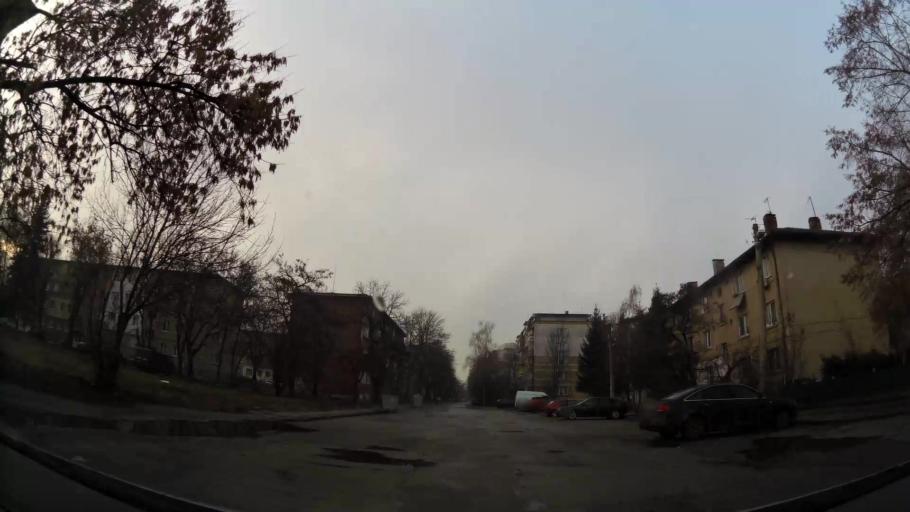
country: BG
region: Sofia-Capital
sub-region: Stolichna Obshtina
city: Sofia
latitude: 42.7304
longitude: 23.3118
